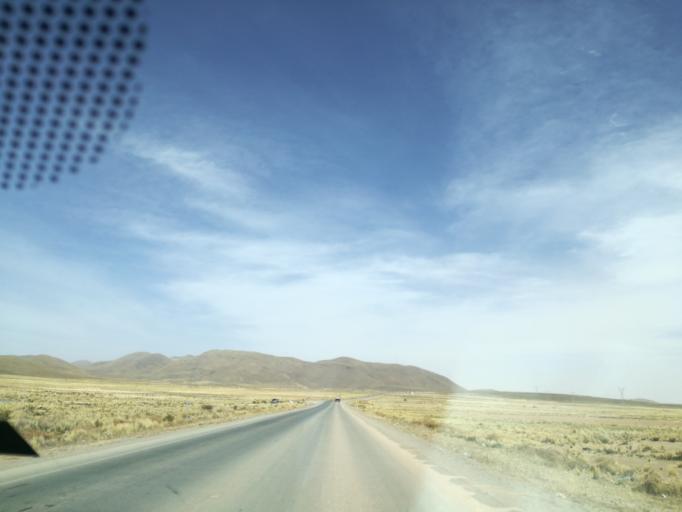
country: BO
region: Oruro
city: Oruro
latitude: -17.8450
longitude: -67.0259
